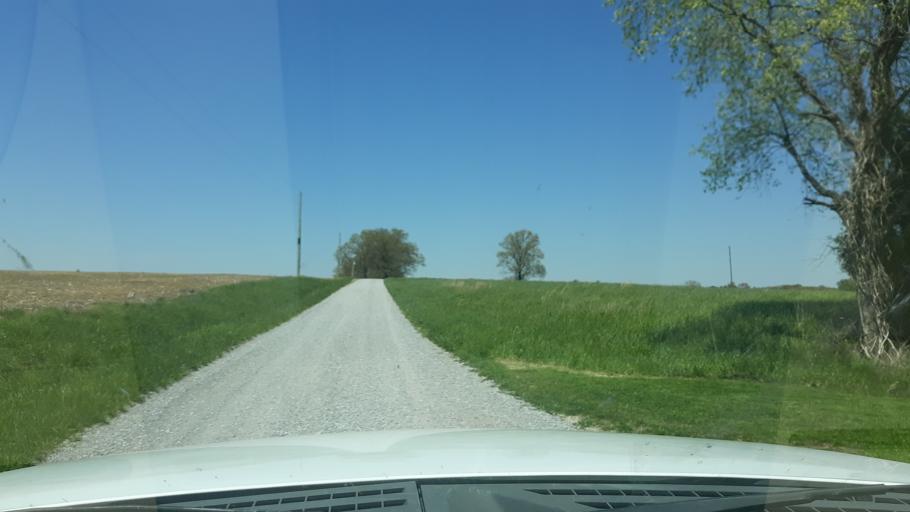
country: US
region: Illinois
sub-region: Saline County
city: Harrisburg
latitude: 37.8831
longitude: -88.6421
